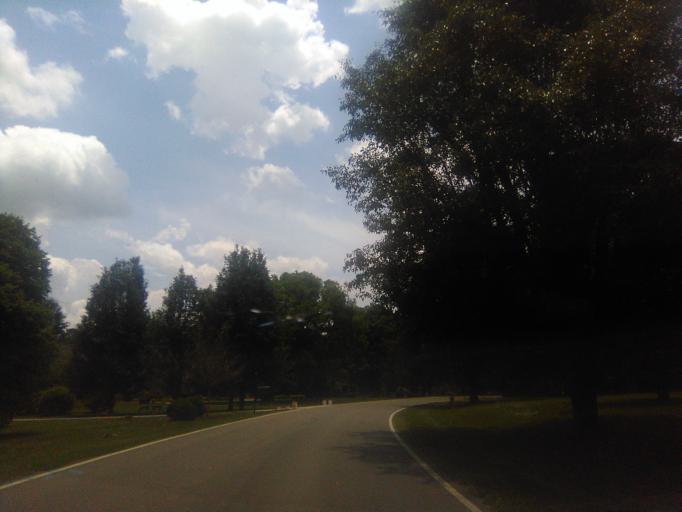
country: US
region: Tennessee
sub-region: Davidson County
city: Belle Meade
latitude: 36.0845
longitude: -86.8637
